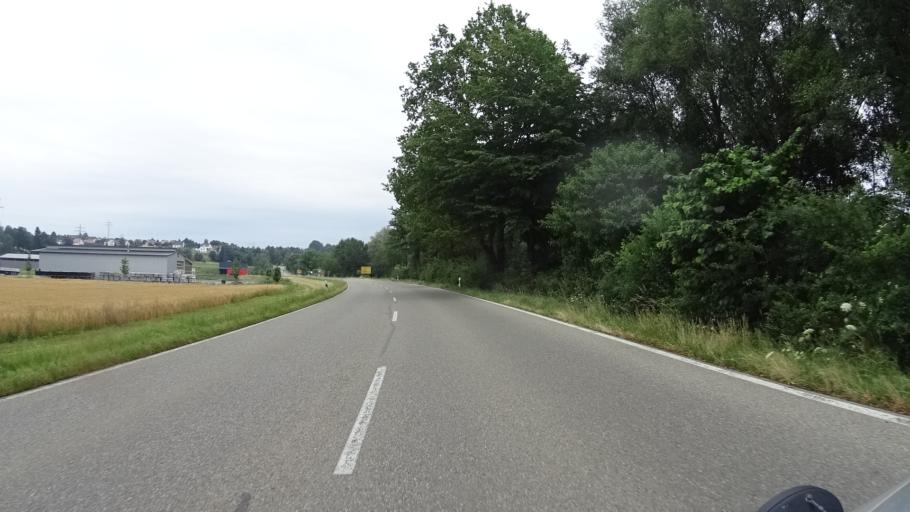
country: DE
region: Bavaria
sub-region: Swabia
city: Kellmunz
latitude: 48.1294
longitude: 10.1203
